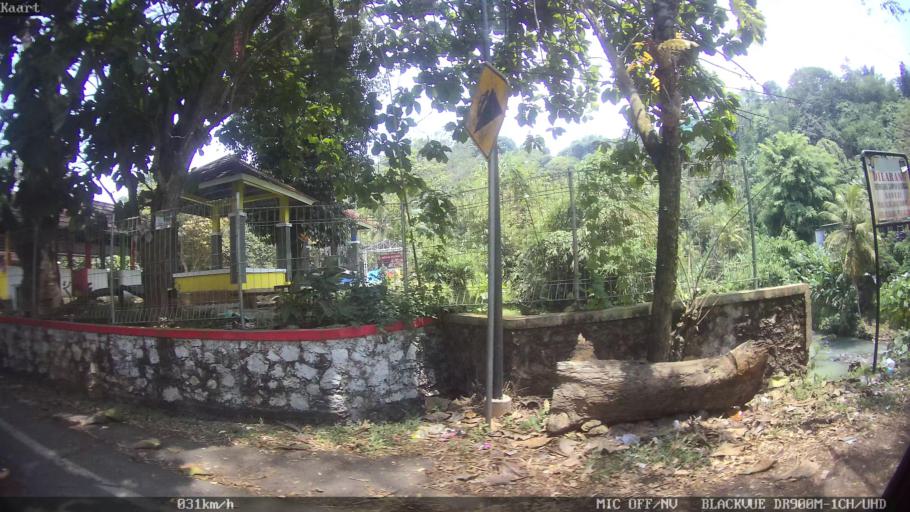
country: ID
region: Lampung
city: Bandarlampung
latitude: -5.4388
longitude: 105.2462
